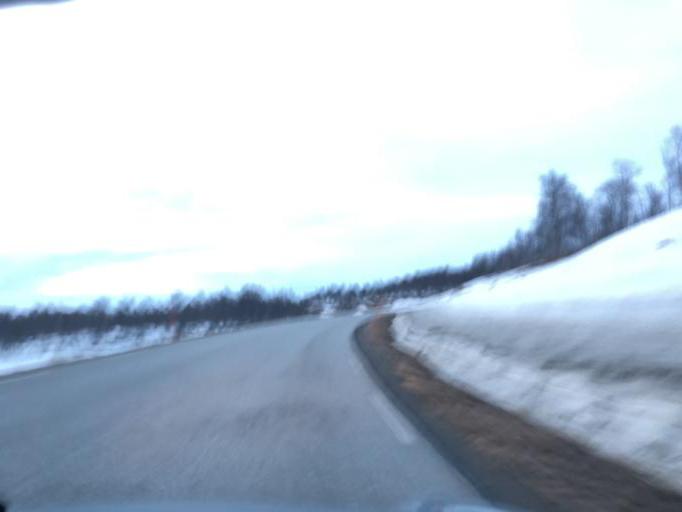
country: NO
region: Sor-Trondelag
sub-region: Tydal
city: Aas
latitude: 62.7264
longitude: 11.8291
